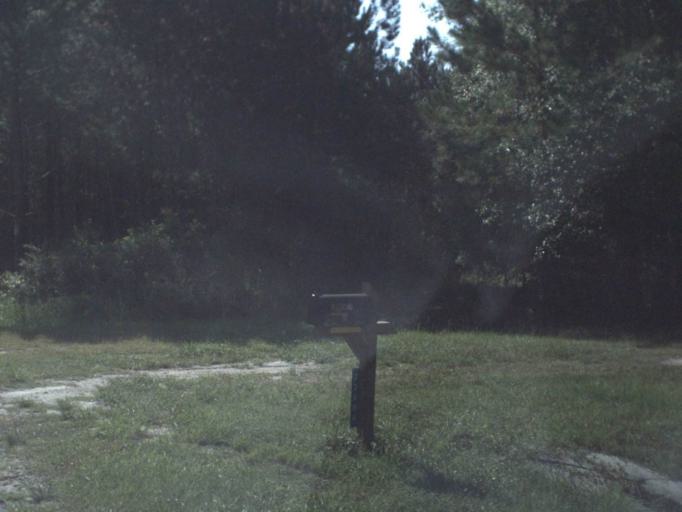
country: US
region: Florida
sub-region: Union County
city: Lake Butler
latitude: 29.9133
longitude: -82.3891
